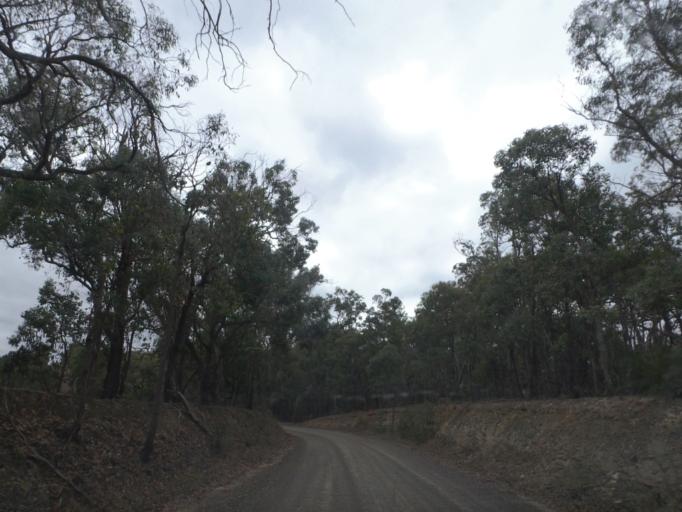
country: AU
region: Victoria
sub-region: Yarra Ranges
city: Yarra Glen
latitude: -37.6708
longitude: 145.3323
